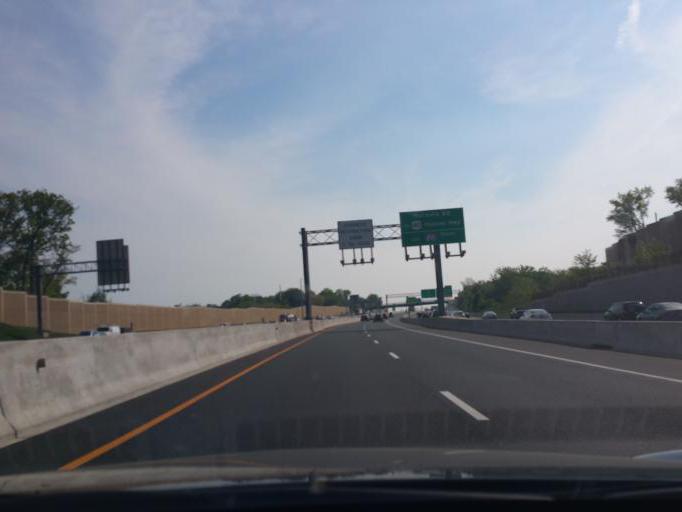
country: US
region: Maryland
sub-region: Baltimore County
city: Rosedale
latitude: 39.3354
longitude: -76.5174
